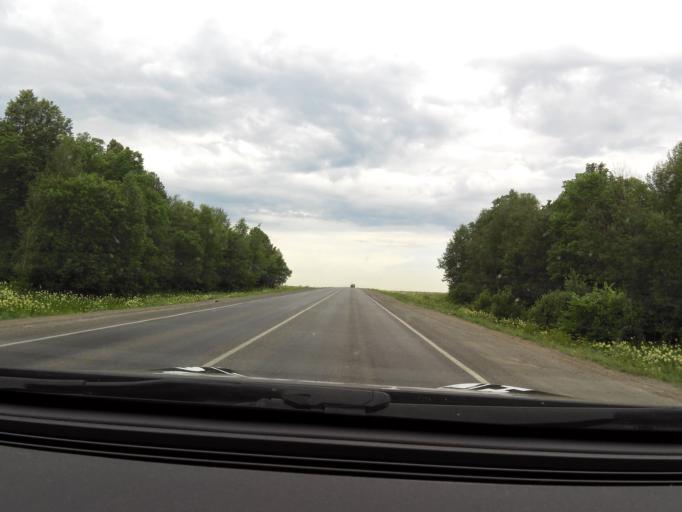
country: RU
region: Bashkortostan
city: Urman
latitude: 54.8174
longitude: 56.8278
